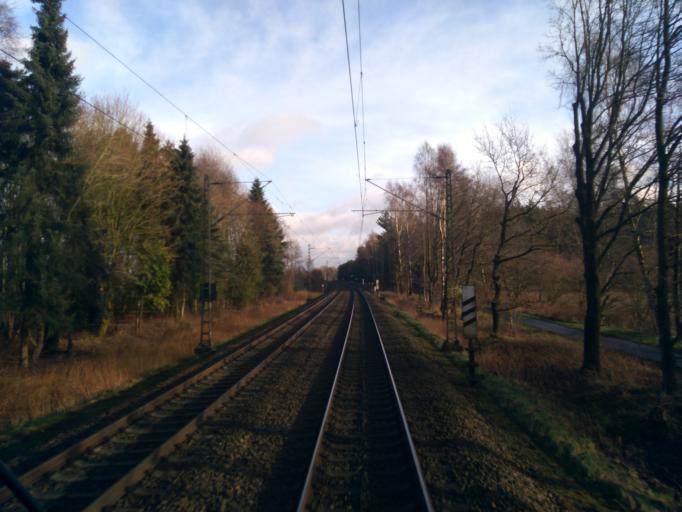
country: DE
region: Lower Saxony
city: Botersen
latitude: 53.1025
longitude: 9.3079
